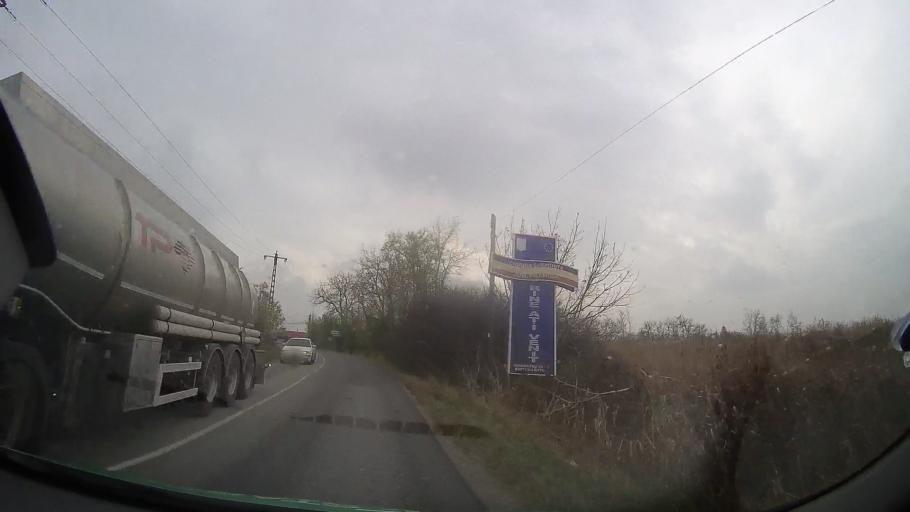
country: RO
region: Prahova
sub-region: Comuna Gherghita
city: Gherghita
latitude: 44.8016
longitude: 26.2668
